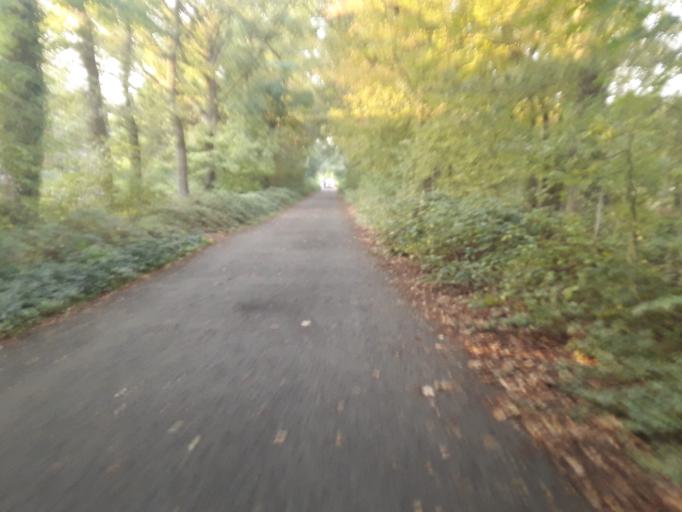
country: DE
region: North Rhine-Westphalia
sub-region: Regierungsbezirk Munster
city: Muenster
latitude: 51.9239
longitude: 7.6601
